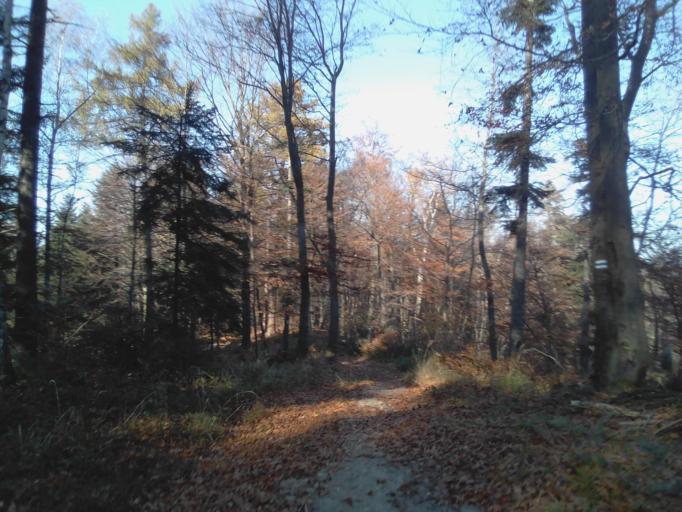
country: PL
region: Subcarpathian Voivodeship
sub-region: Powiat krosnienski
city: Leki
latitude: 49.8216
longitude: 21.6975
